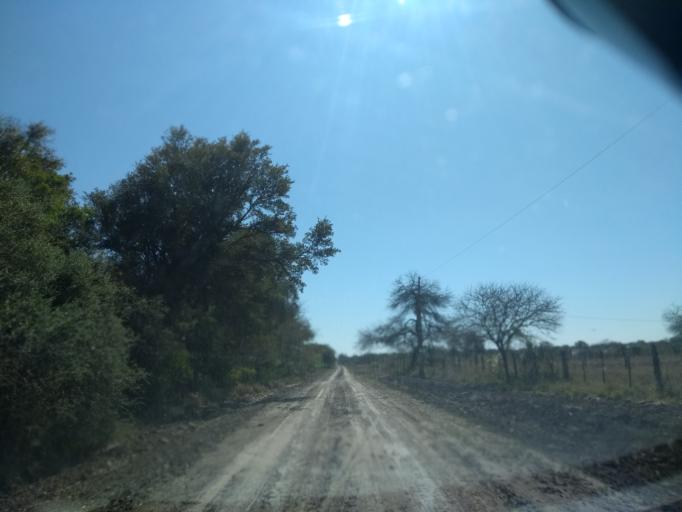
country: AR
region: Chaco
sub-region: Departamento de Quitilipi
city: Quitilipi
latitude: -26.7364
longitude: -60.2343
